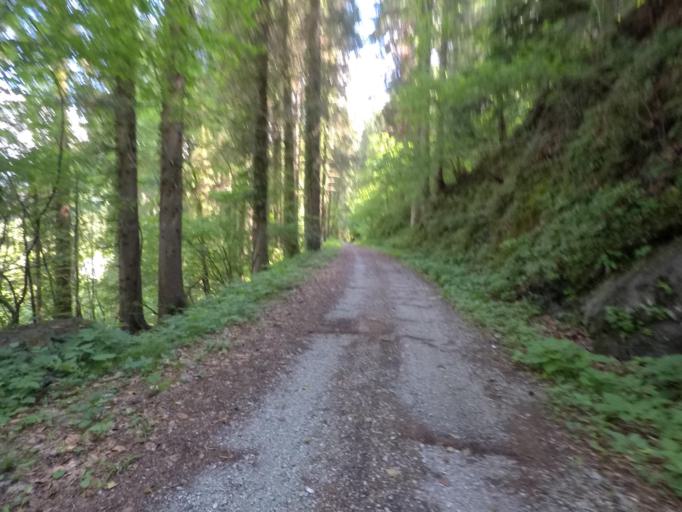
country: IT
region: Friuli Venezia Giulia
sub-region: Provincia di Udine
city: Ovaro
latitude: 46.4639
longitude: 12.8745
